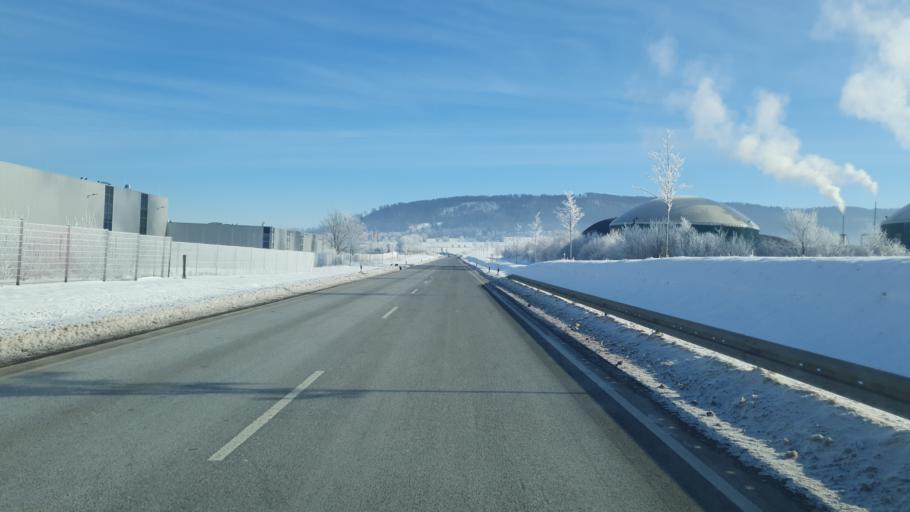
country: DE
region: Lower Saxony
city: Aerzen
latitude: 52.0353
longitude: 9.2525
